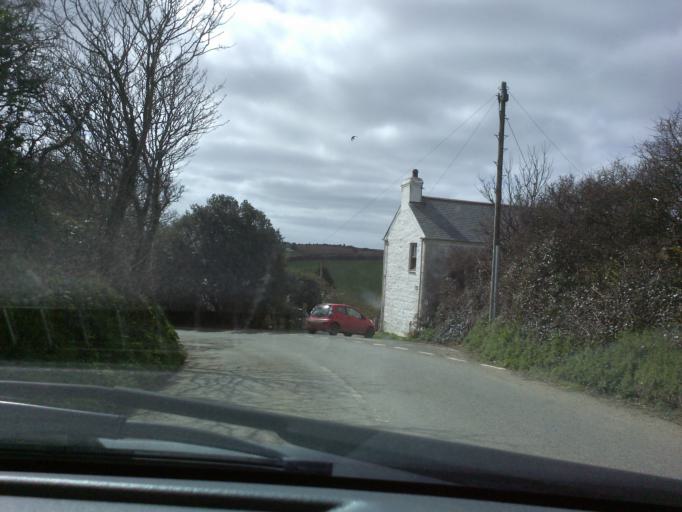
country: GB
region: England
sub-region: Cornwall
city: St. Buryan
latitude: 50.0597
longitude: -5.6074
